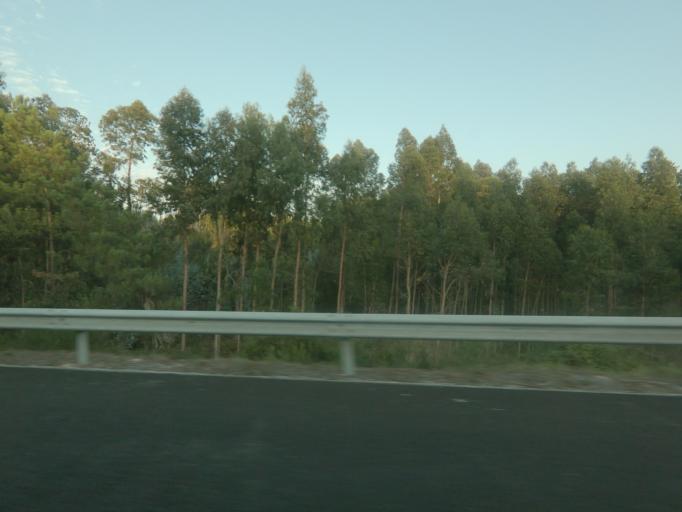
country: PT
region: Leiria
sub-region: Leiria
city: Caranguejeira
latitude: 39.8017
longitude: -8.7256
